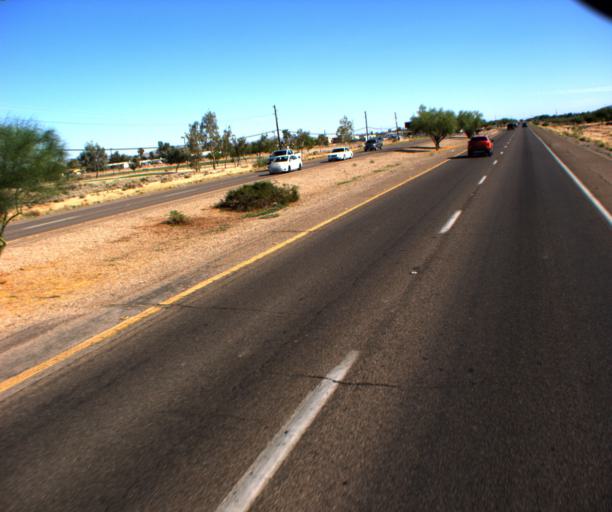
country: US
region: Arizona
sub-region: Pinal County
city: Casa Grande
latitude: 32.9282
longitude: -111.7567
